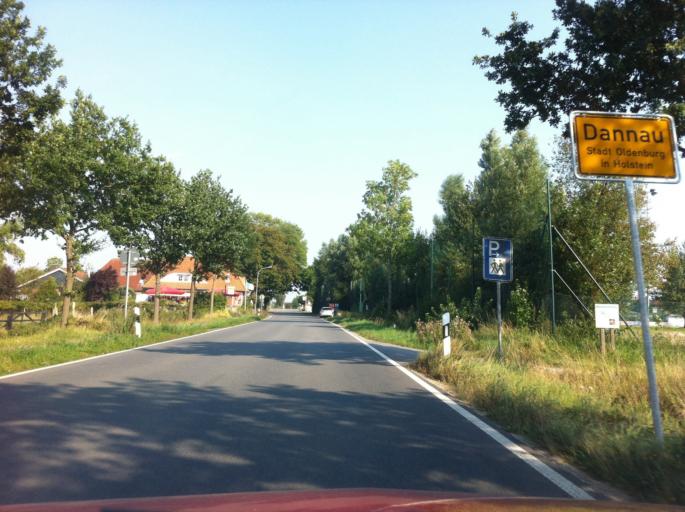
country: DE
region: Schleswig-Holstein
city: Harmsdorf
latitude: 54.3032
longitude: 10.8451
